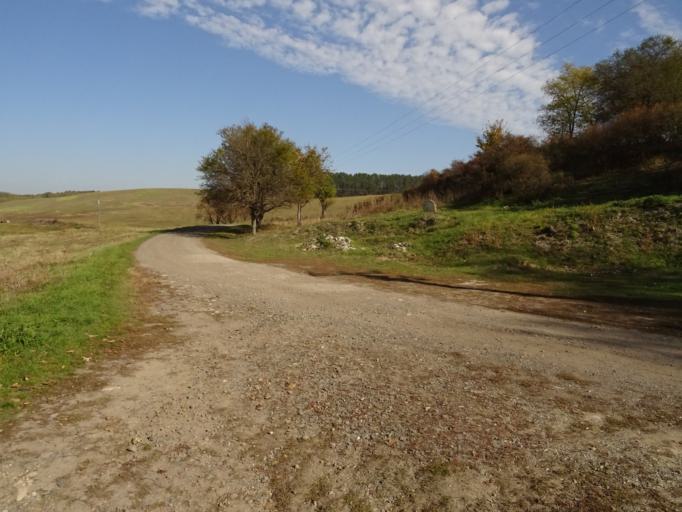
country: HU
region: Nograd
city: Matraverebely
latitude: 48.0342
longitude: 19.7545
